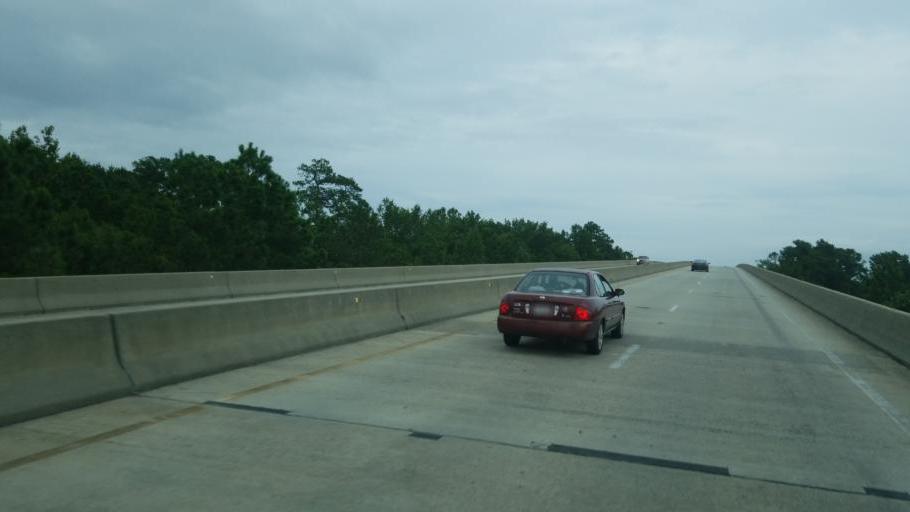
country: US
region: North Carolina
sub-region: Currituck County
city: Currituck
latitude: 36.3428
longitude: -75.9568
